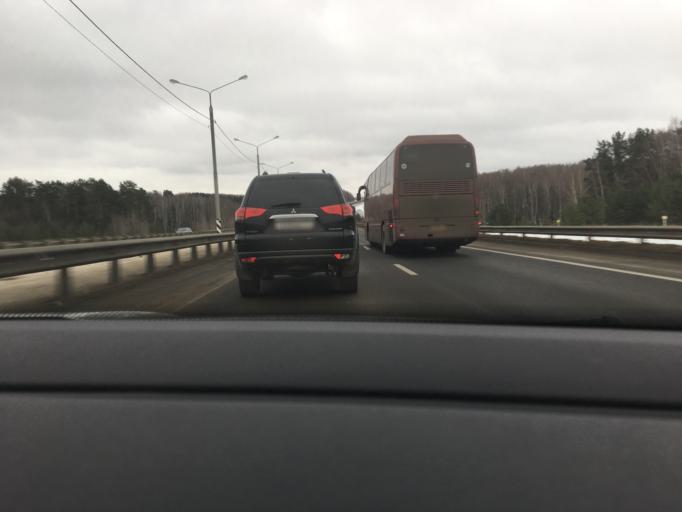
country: RU
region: Tula
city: Zaokskiy
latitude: 54.8212
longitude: 37.4731
